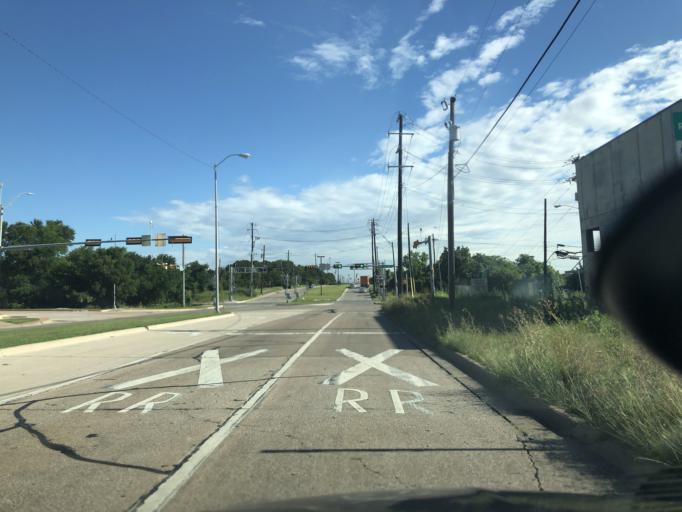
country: US
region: Texas
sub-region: Tarrant County
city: Euless
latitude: 32.8156
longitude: -97.0304
